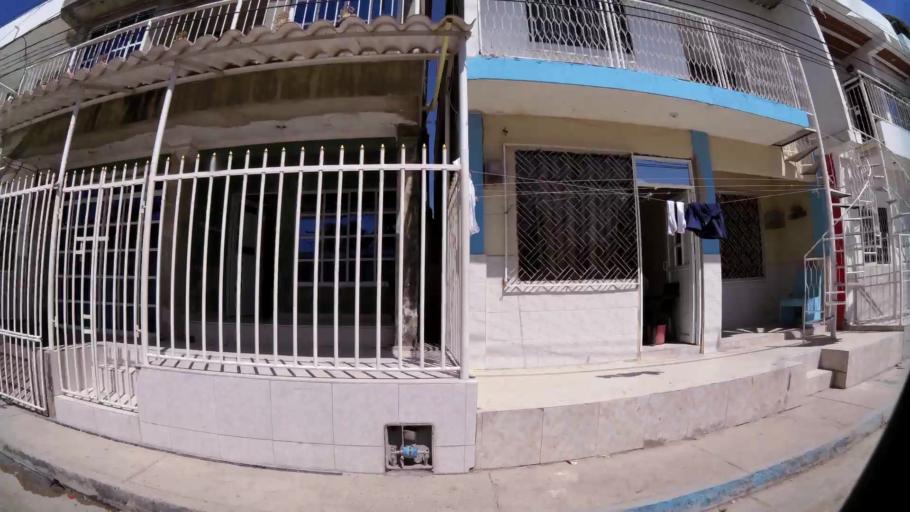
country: CO
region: Bolivar
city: Cartagena
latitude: 10.3869
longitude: -75.5055
